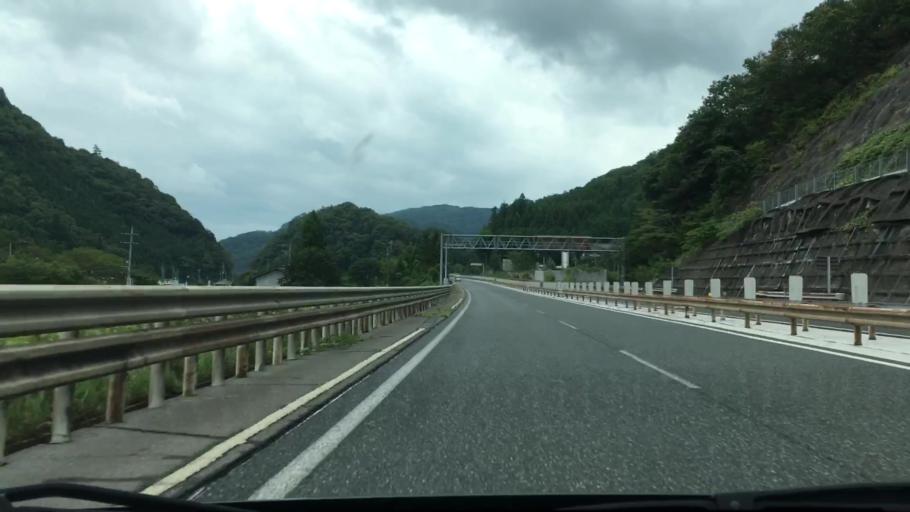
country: JP
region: Okayama
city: Niimi
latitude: 35.0036
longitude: 133.4740
